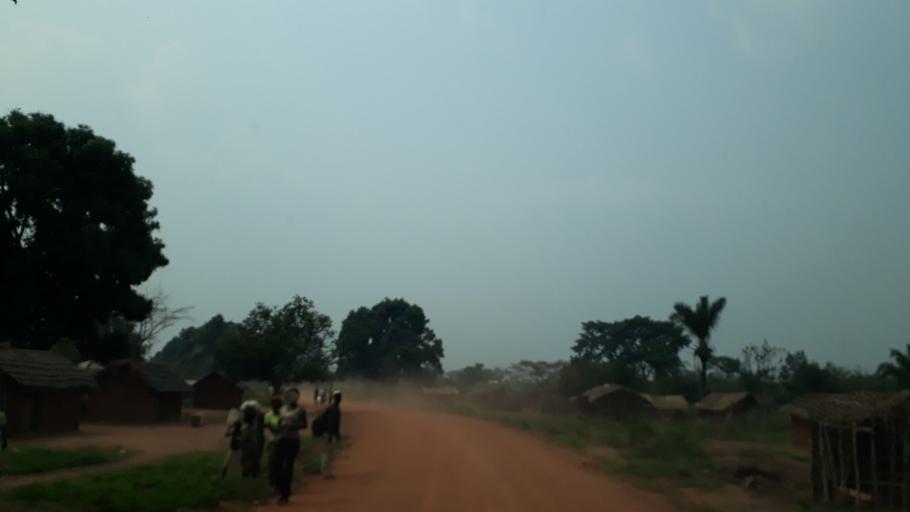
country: CD
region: Kasai-Occidental
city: Tshikapa
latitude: -6.4670
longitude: 20.4640
